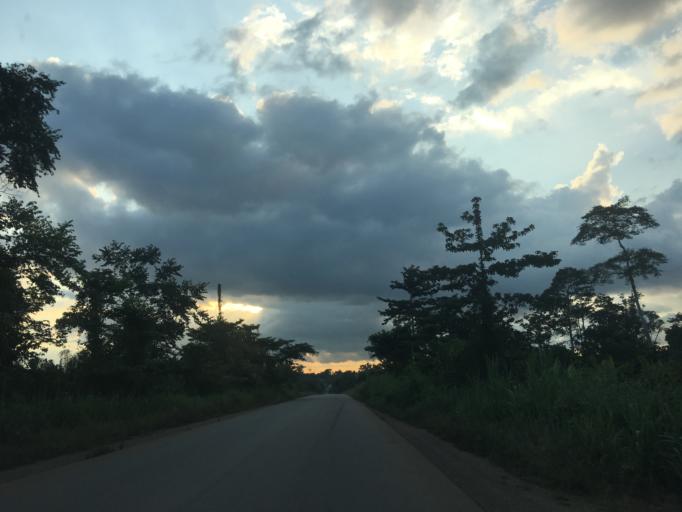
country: GH
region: Western
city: Bibiani
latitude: 6.7165
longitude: -2.4639
